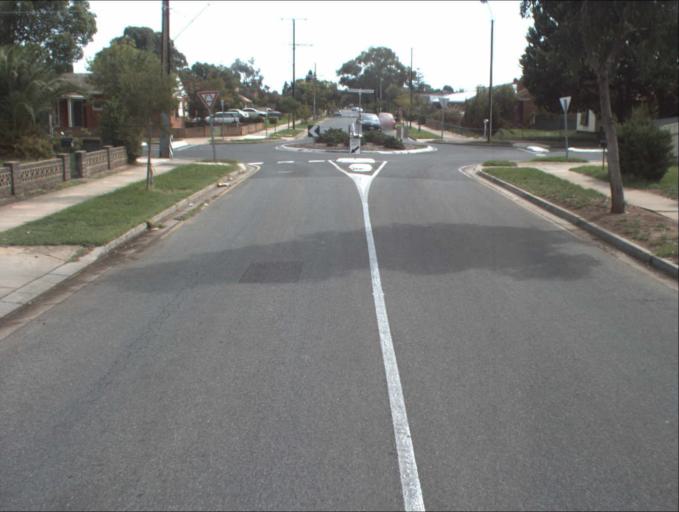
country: AU
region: South Australia
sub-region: Port Adelaide Enfield
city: Enfield
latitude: -34.8525
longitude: 138.5962
